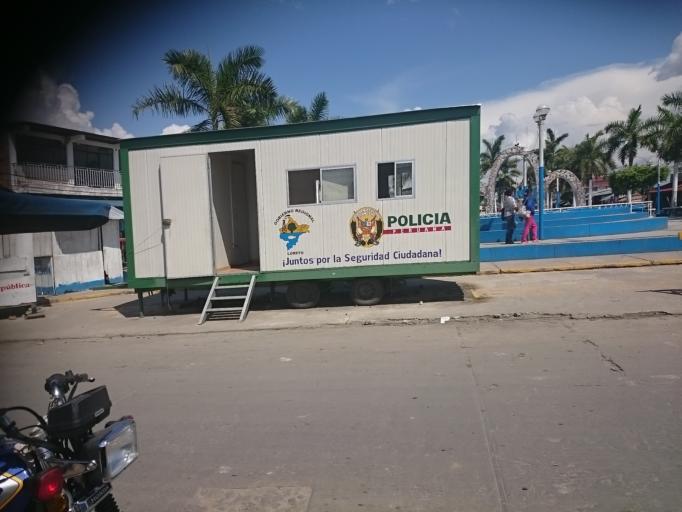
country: PE
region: Loreto
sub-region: Provincia de Maynas
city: Iquitos
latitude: -3.7037
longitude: -73.2489
